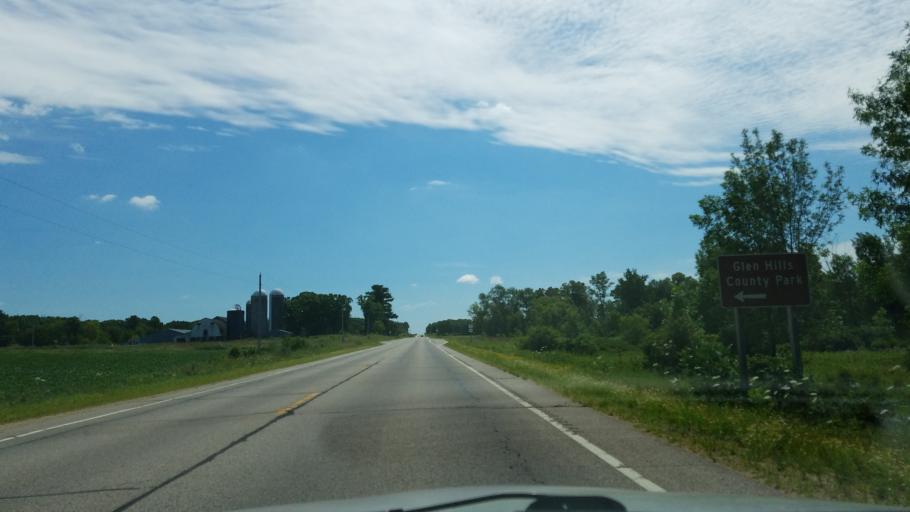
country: US
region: Wisconsin
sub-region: Saint Croix County
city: Glenwood City
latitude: 44.9899
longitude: -92.1966
